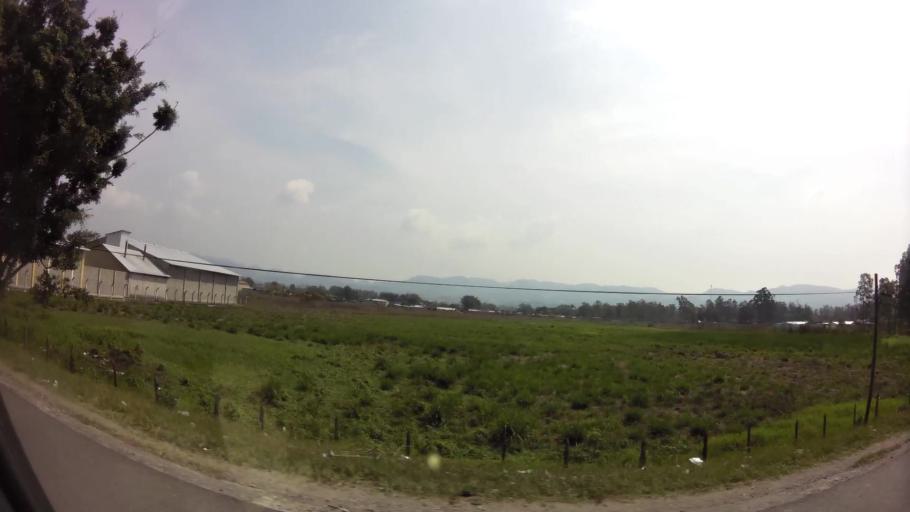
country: HN
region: Comayagua
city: Siguatepeque
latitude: 14.5813
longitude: -87.8427
